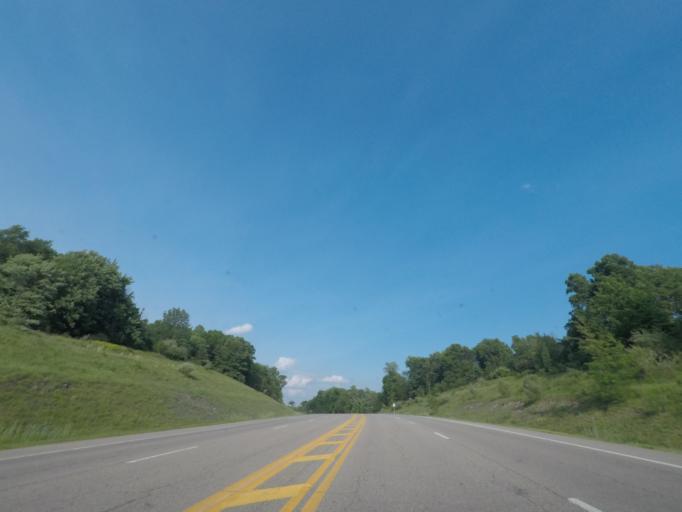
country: US
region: New York
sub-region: Orange County
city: Orange Lake
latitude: 41.4967
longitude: -74.1258
